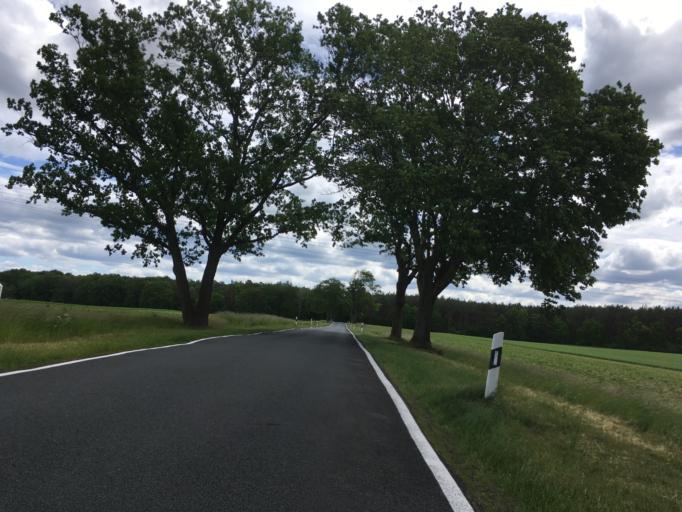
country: DE
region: Brandenburg
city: Melchow
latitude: 52.7388
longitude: 13.7344
